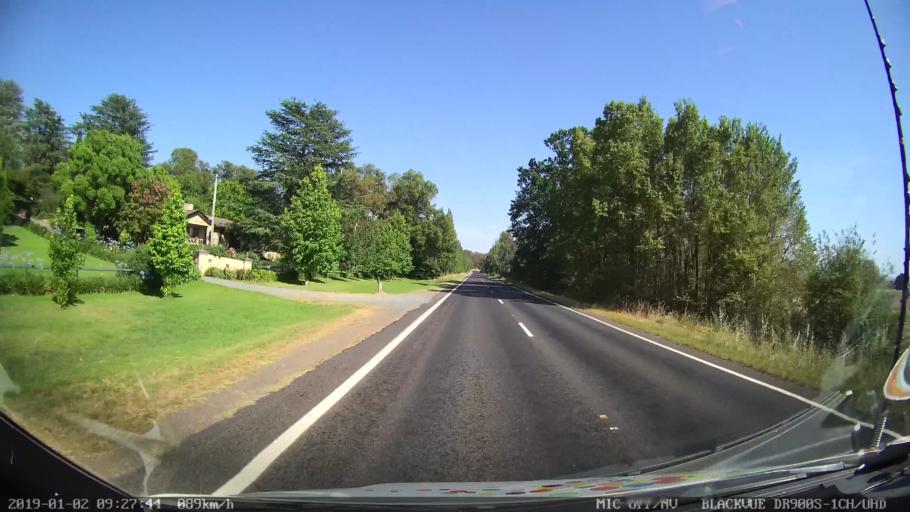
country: AU
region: New South Wales
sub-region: Tumut Shire
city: Tumut
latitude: -35.3588
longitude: 148.2551
